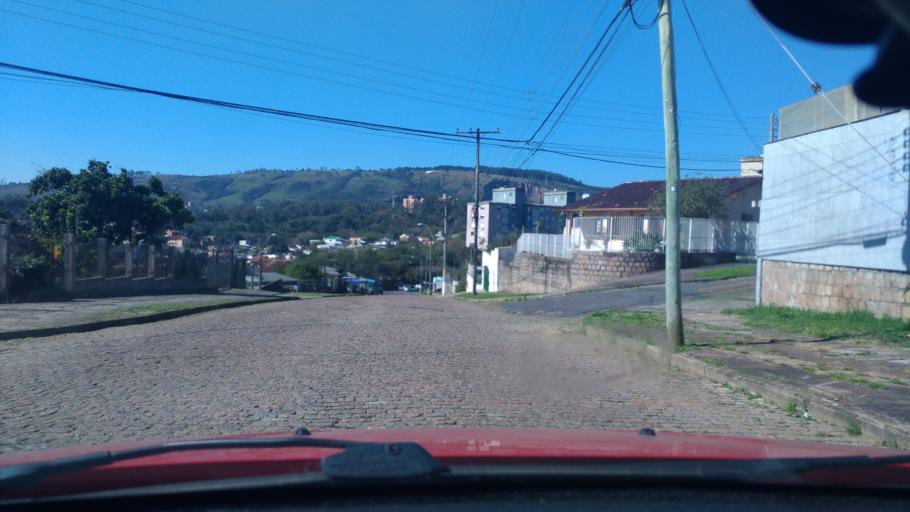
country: BR
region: Rio Grande do Sul
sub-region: Porto Alegre
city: Porto Alegre
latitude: -30.0362
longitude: -51.1453
